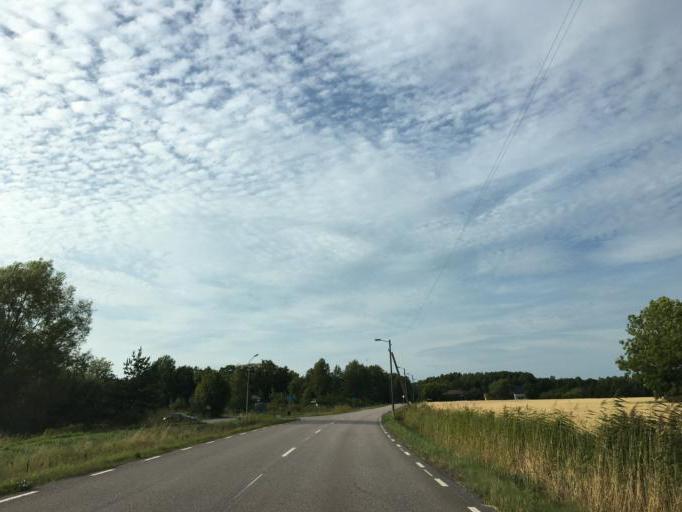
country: SE
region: Soedermanland
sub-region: Eskilstuna Kommun
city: Torshalla
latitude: 59.4426
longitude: 16.4530
